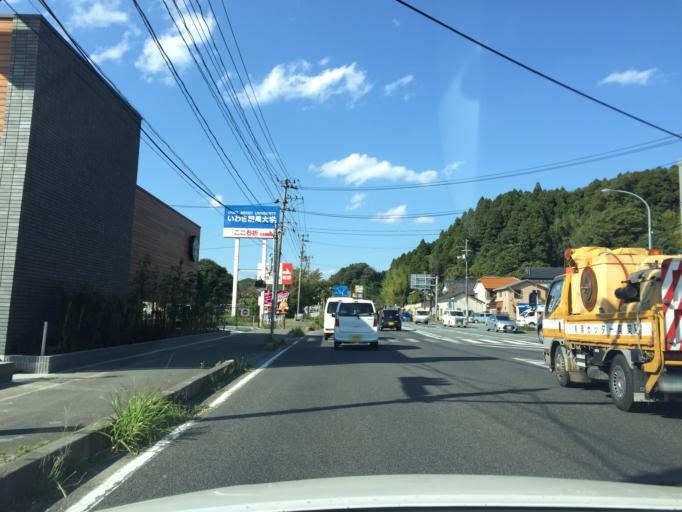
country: JP
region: Fukushima
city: Iwaki
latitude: 37.0165
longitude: 140.9031
